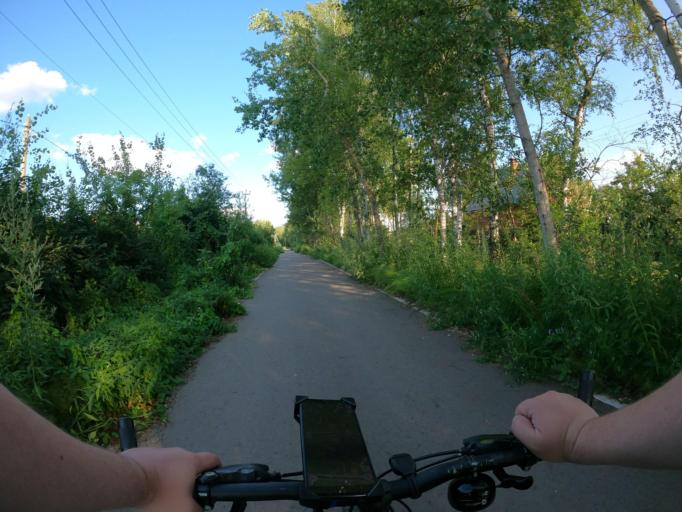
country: RU
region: Moskovskaya
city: Beloozerskiy
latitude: 55.4835
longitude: 38.4117
